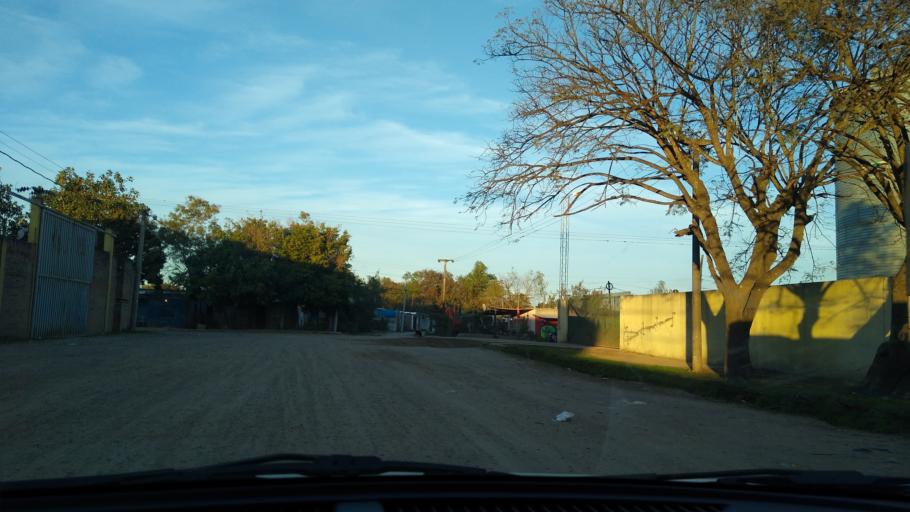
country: AR
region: Chaco
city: Resistencia
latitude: -27.4772
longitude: -58.9630
